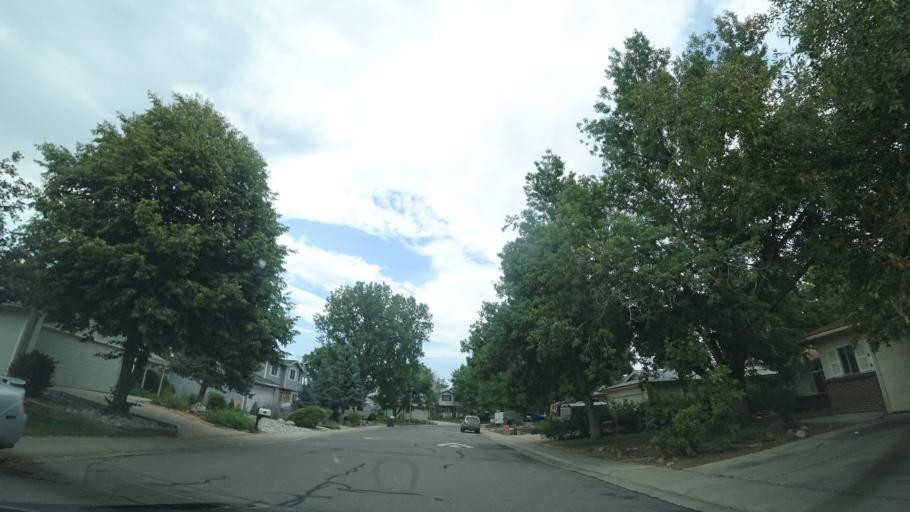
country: US
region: Colorado
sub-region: Jefferson County
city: Lakewood
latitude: 39.7059
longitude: -105.0995
